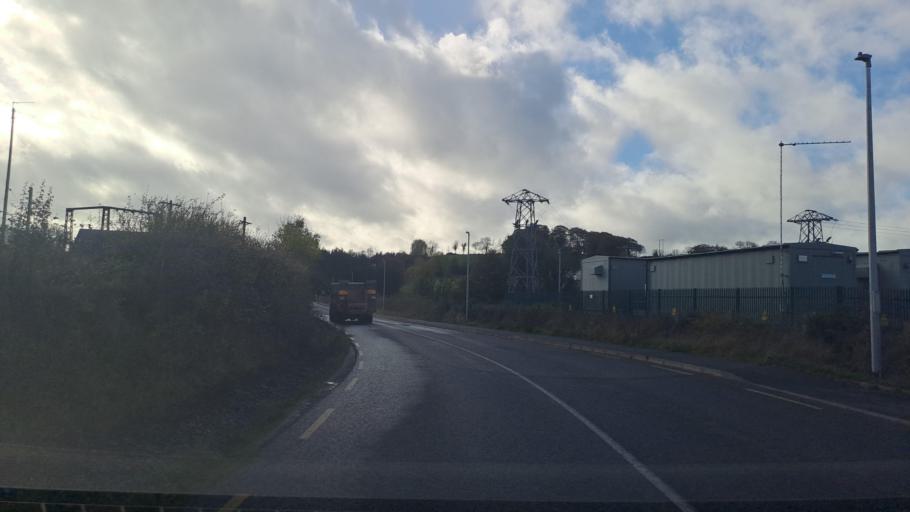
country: IE
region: Ulster
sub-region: County Monaghan
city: Monaghan
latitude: 54.1214
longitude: -6.9071
